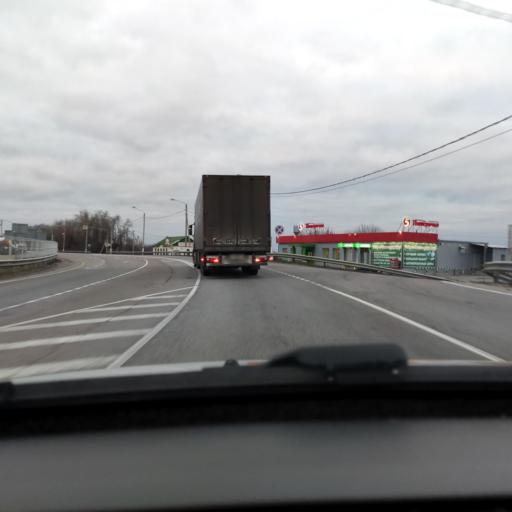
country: RU
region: Lipetsk
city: Khlevnoye
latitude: 52.2667
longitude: 39.1684
